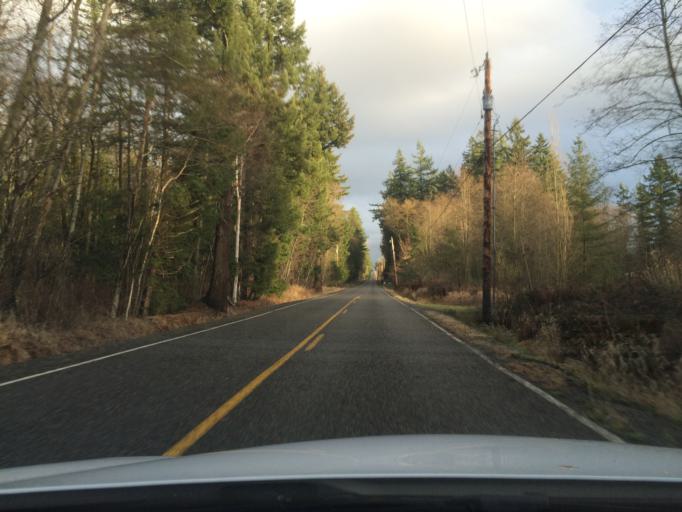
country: CA
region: British Columbia
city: Langley
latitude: 48.9935
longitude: -122.5951
